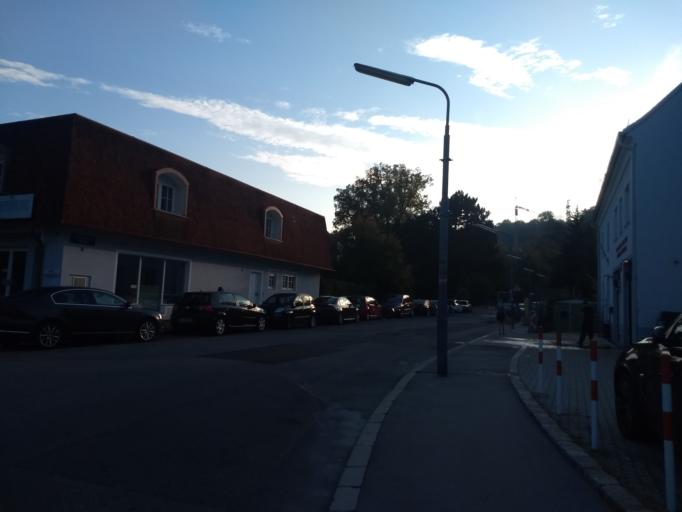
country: AT
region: Lower Austria
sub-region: Politischer Bezirk Wien-Umgebung
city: Purkersdorf
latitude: 48.2084
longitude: 16.2126
